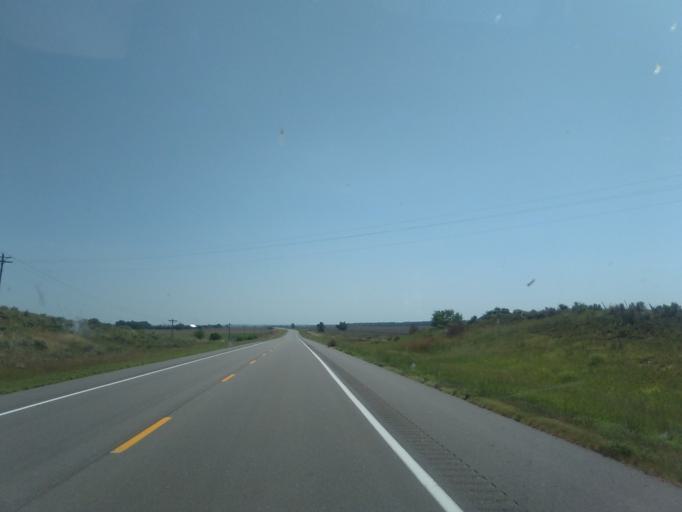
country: US
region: Nebraska
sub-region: Dundy County
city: Benkelman
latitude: 40.0806
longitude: -101.4873
